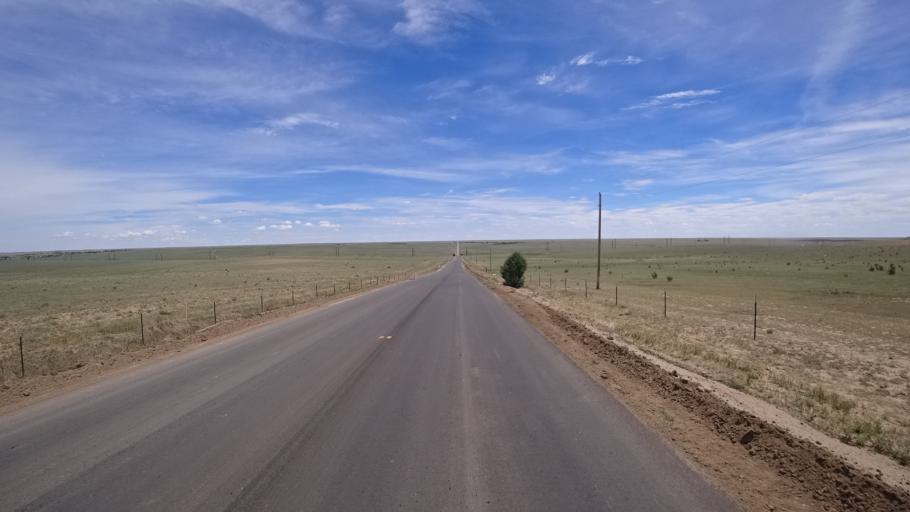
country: US
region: Colorado
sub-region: El Paso County
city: Fountain
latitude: 38.6939
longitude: -104.6423
